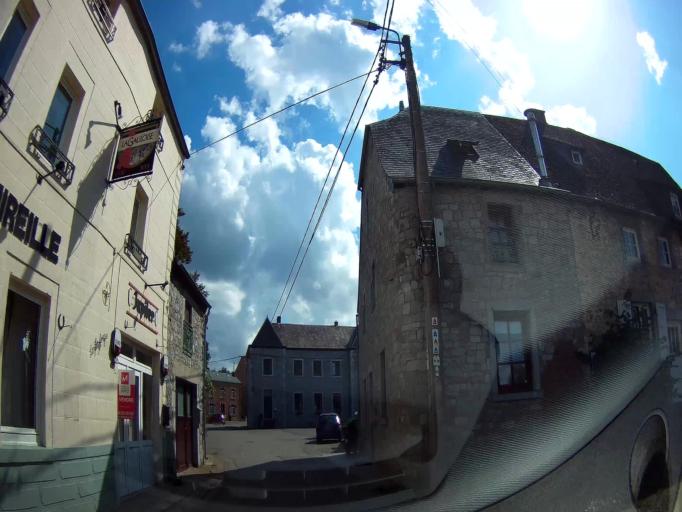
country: BE
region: Wallonia
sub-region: Province de Namur
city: Profondeville
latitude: 50.3434
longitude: 4.8410
